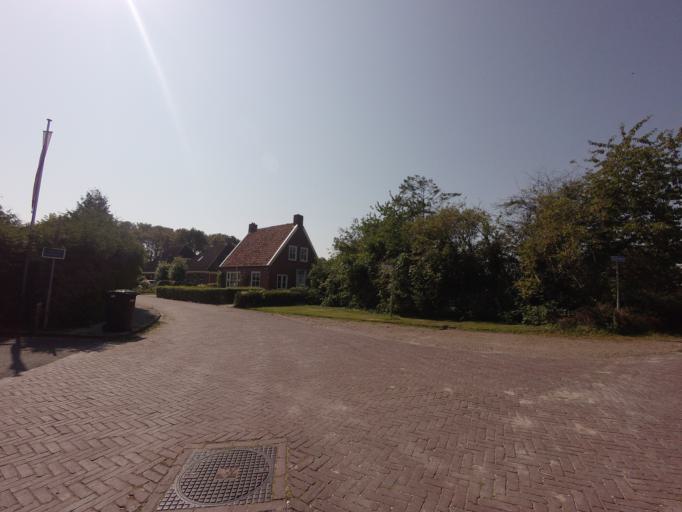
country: NL
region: Groningen
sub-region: Gemeente De Marne
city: Ulrum
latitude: 53.3600
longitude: 6.2902
